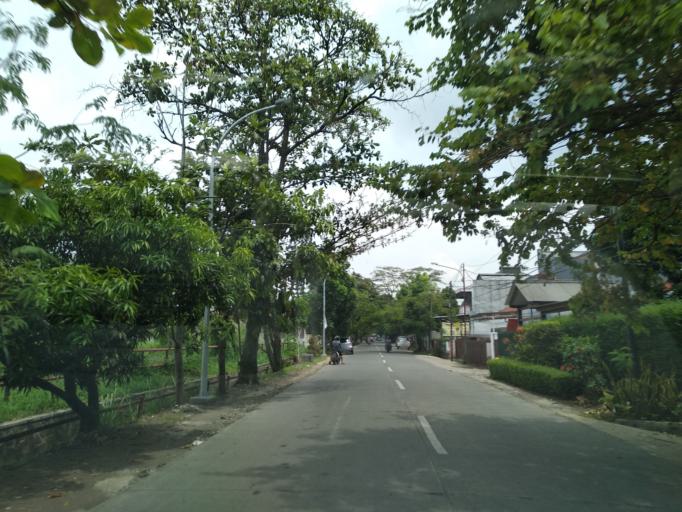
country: ID
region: West Java
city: Bandung
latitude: -6.9453
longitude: 107.6344
